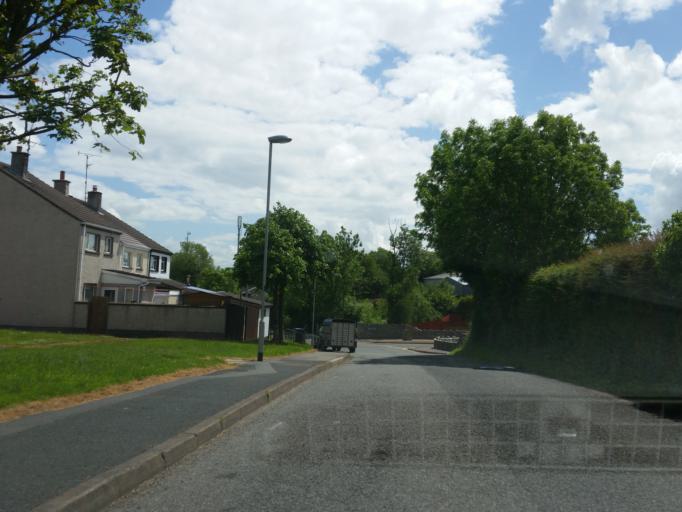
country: GB
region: Northern Ireland
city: Fivemiletown
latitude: 54.3760
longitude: -7.3157
